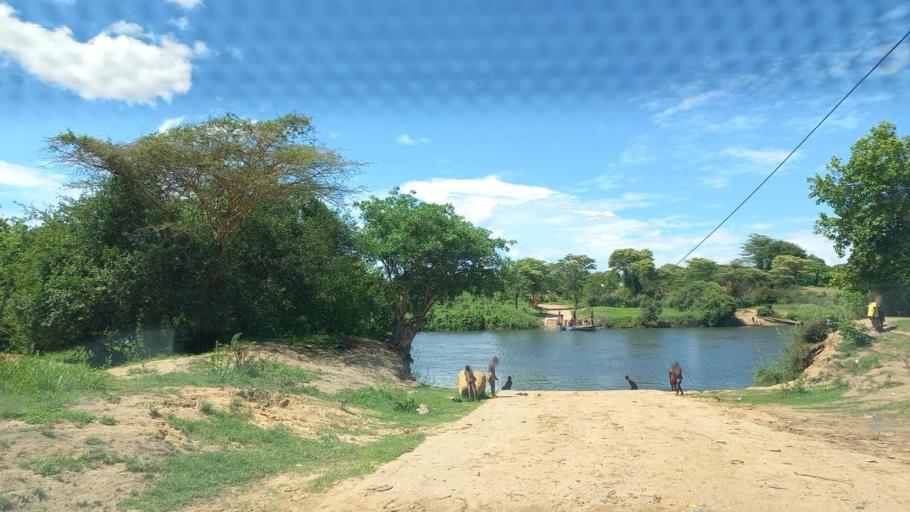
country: ZM
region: North-Western
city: Kabompo
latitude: -13.6154
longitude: 24.2093
